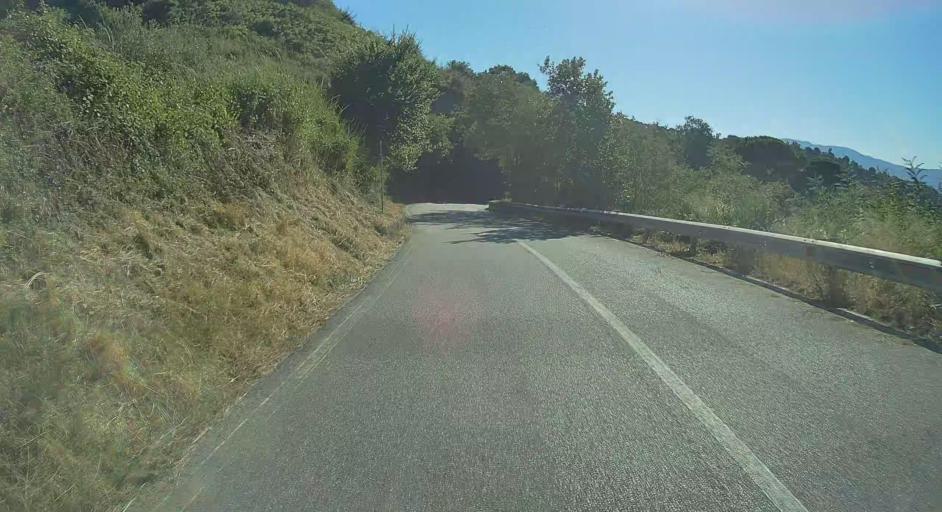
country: IT
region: Sicily
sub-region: Messina
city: Oliveri
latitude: 38.1378
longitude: 15.0391
